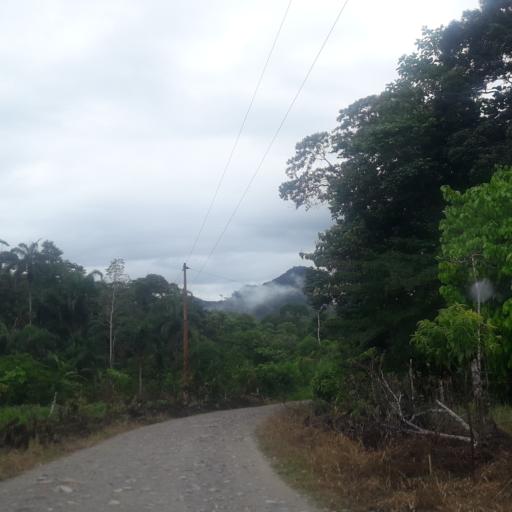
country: EC
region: Napo
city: Archidona
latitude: -0.9133
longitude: -77.8230
